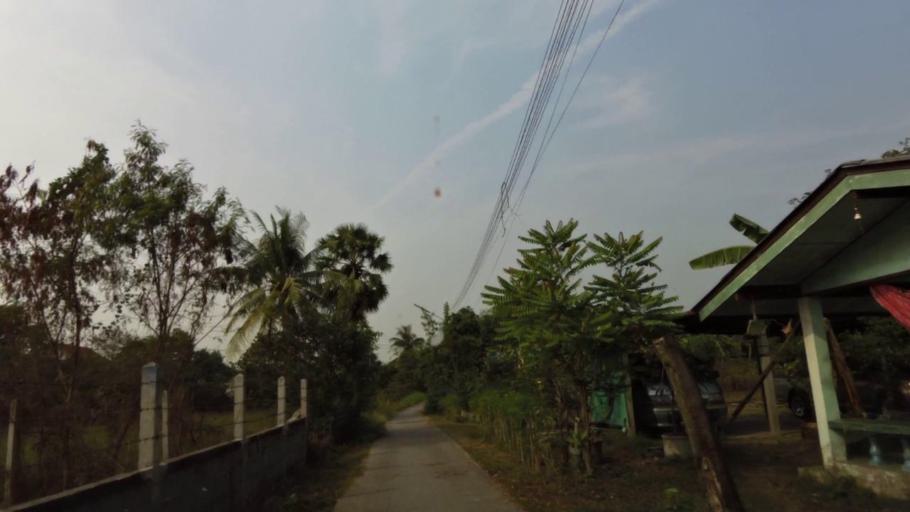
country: TH
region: Phra Nakhon Si Ayutthaya
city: Phra Nakhon Si Ayutthaya
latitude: 14.3431
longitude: 100.5694
